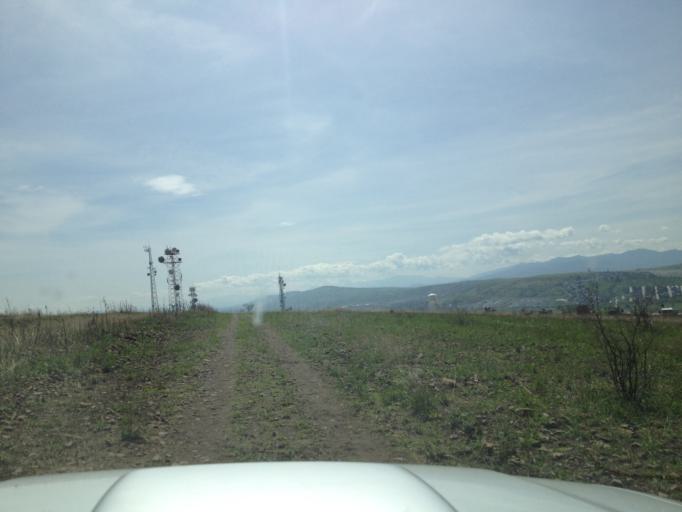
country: MX
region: Michoacan
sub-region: Tarimbaro
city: San Bernabe de las Canteras
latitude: 19.7689
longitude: -101.1688
